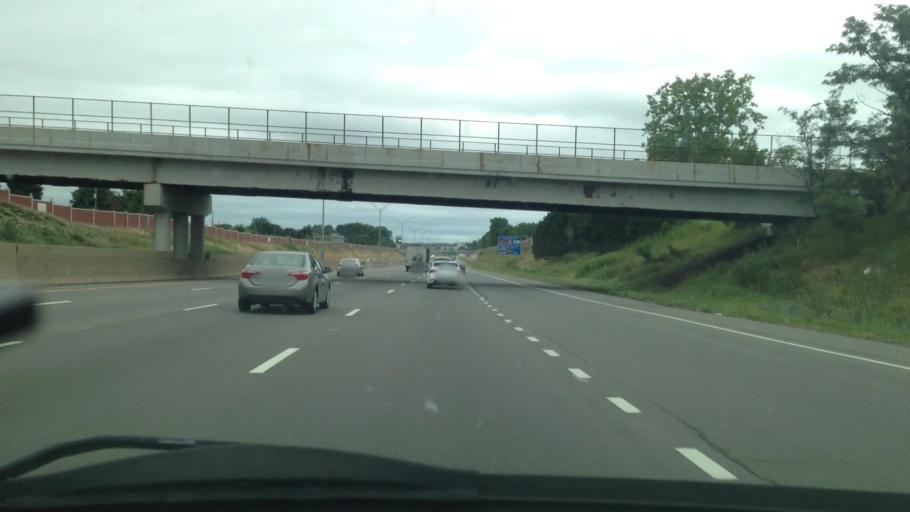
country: US
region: Ohio
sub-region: Cuyahoga County
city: Brooklyn
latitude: 41.4225
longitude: -81.7400
